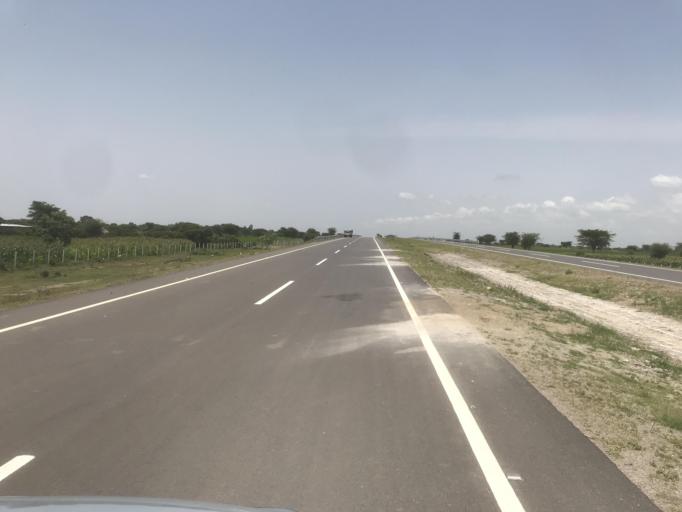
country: ET
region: Oromiya
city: Mojo
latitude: 8.2697
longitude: 38.9072
